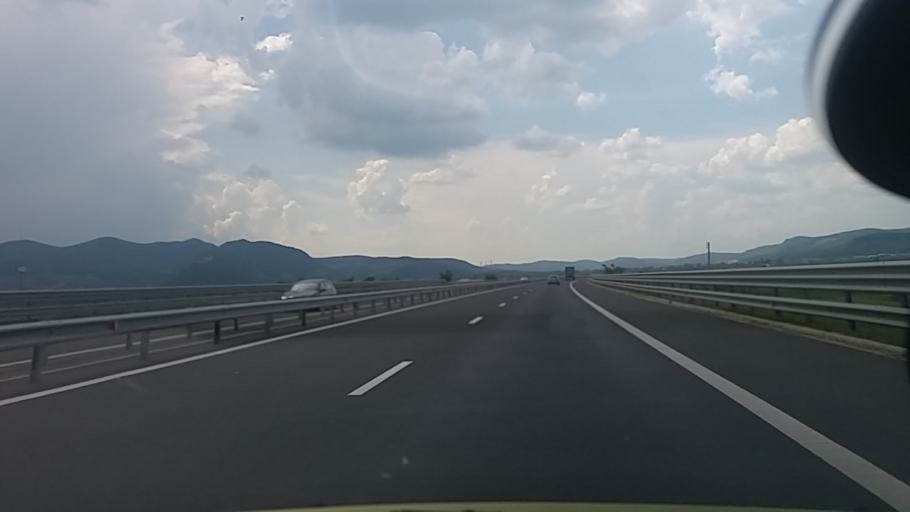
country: RO
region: Hunedoara
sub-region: Comuna Harau
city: Harau
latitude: 45.8938
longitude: 22.9476
